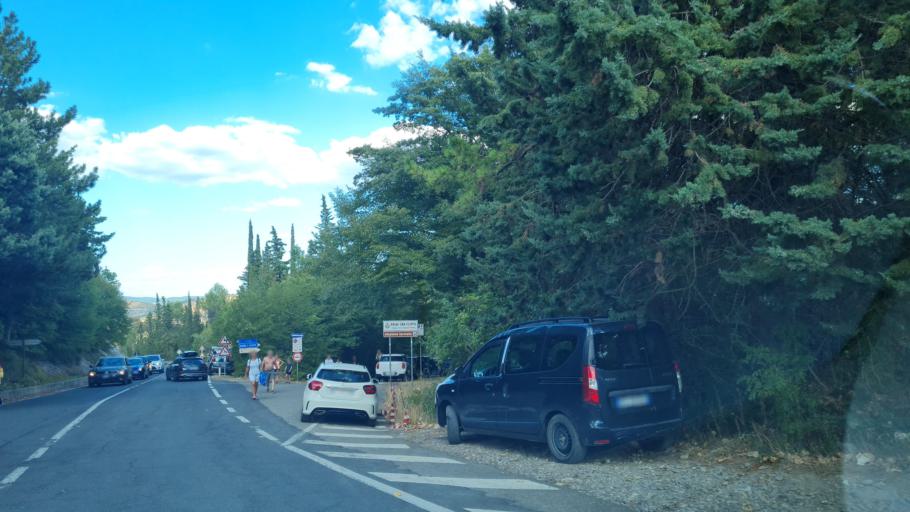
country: IT
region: Tuscany
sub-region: Provincia di Siena
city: Abbadia San Salvatore
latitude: 42.9265
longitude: 11.7002
